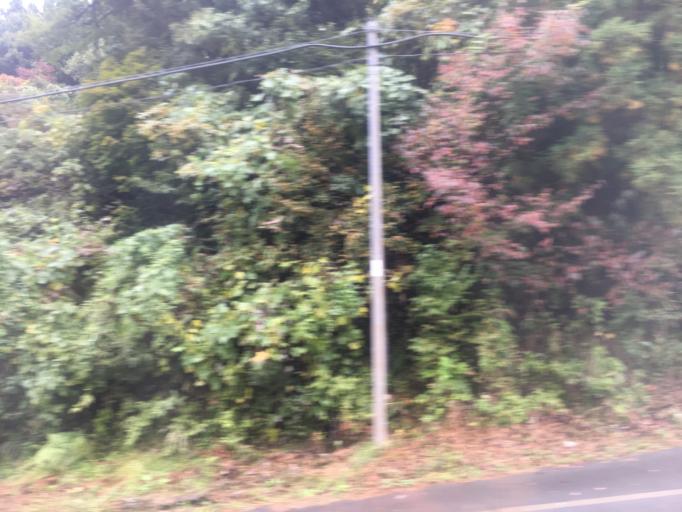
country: JP
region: Niigata
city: Murakami
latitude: 38.0773
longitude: 139.6622
